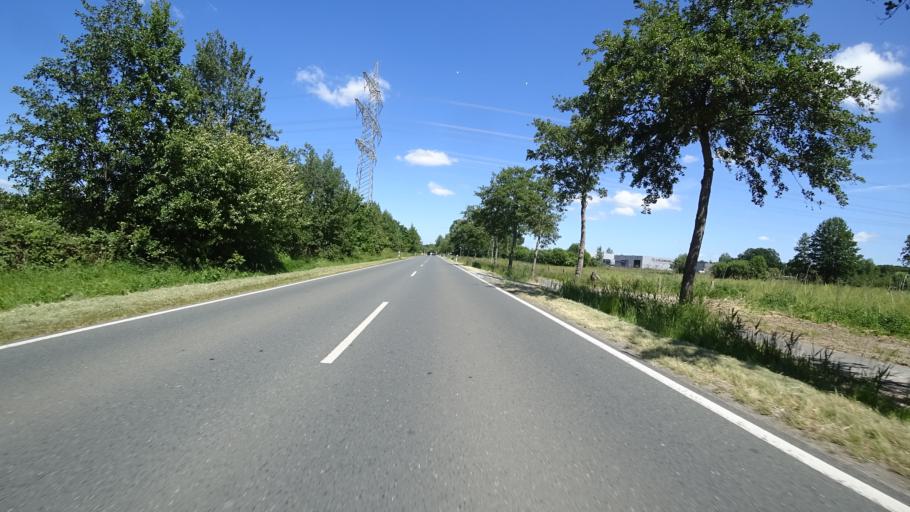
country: DE
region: North Rhine-Westphalia
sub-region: Regierungsbezirk Detmold
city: Guetersloh
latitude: 51.9275
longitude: 8.4265
